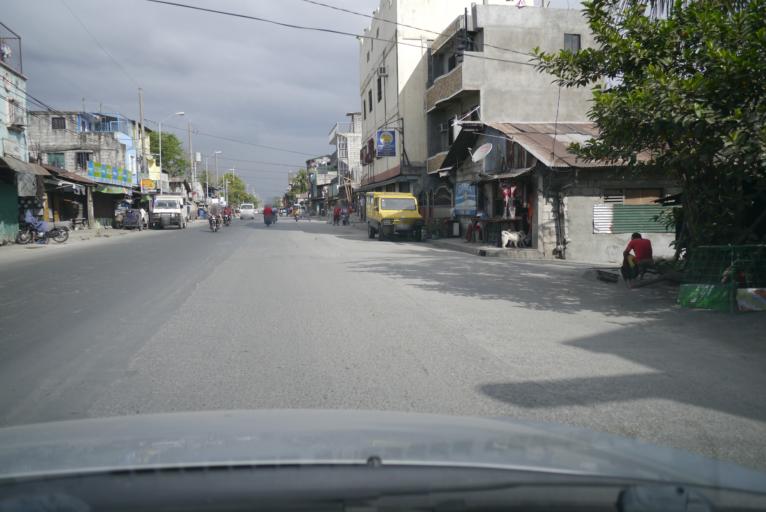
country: PH
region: Calabarzon
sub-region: Province of Rizal
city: Taytay
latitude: 14.5468
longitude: 121.1225
